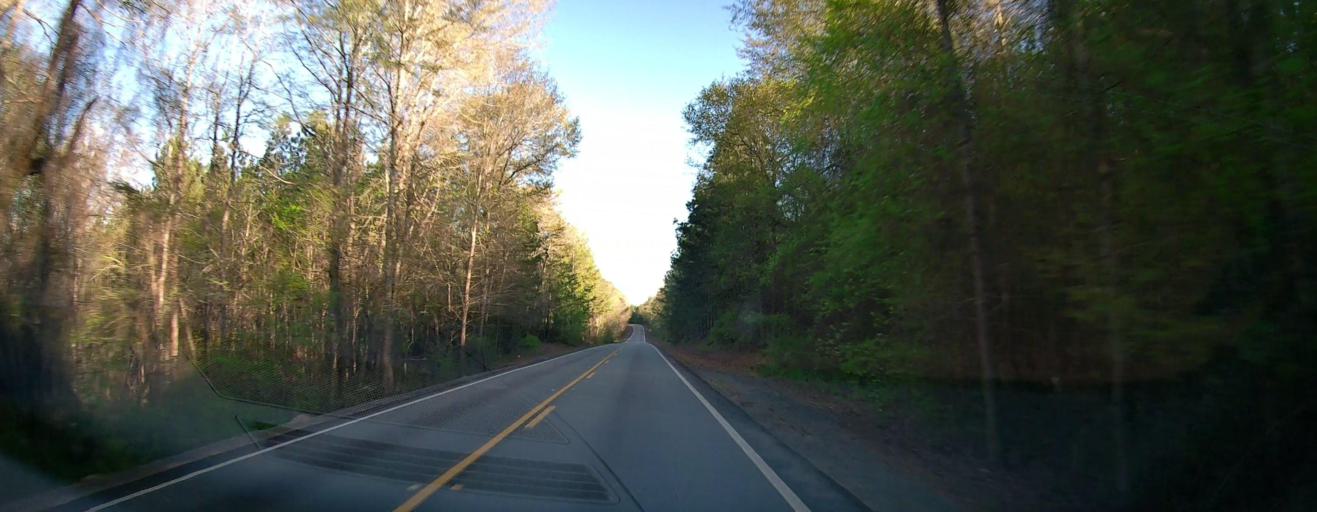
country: US
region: Georgia
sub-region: Wilkinson County
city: Irwinton
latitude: 32.9341
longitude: -83.1471
